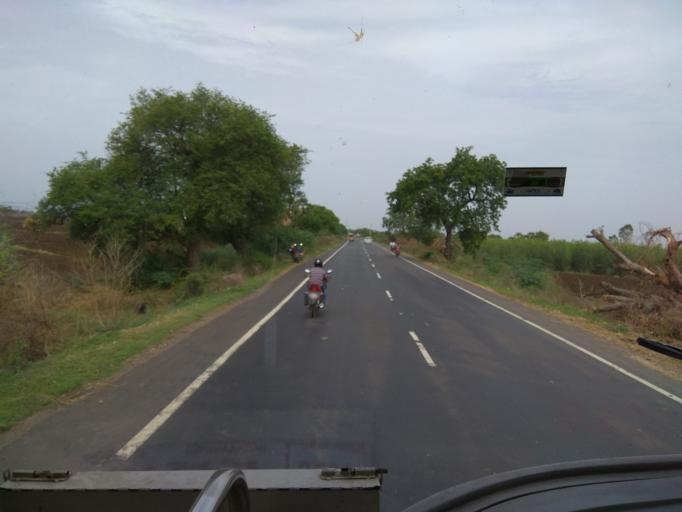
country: IN
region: Andhra Pradesh
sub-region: Guntur
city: Phirangipuram
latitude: 16.2843
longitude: 80.2264
